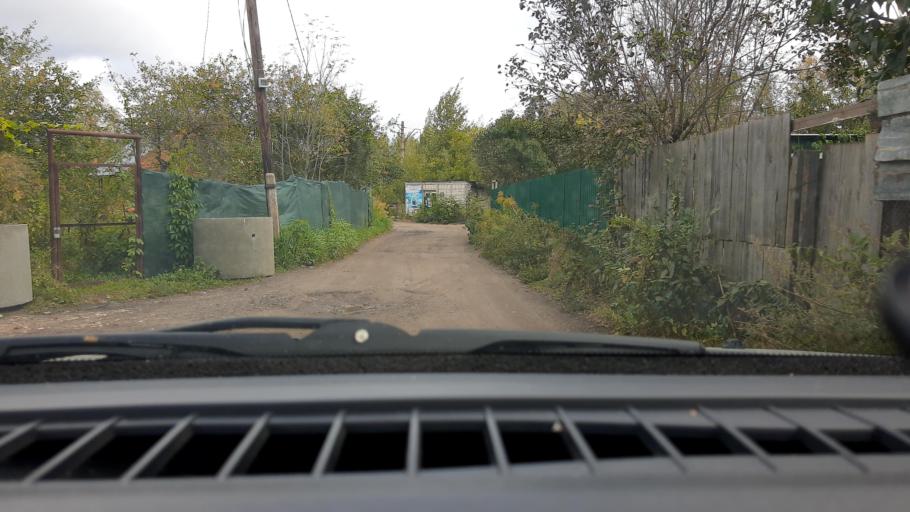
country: RU
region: Nizjnij Novgorod
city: Gorbatovka
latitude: 56.3216
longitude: 43.8389
